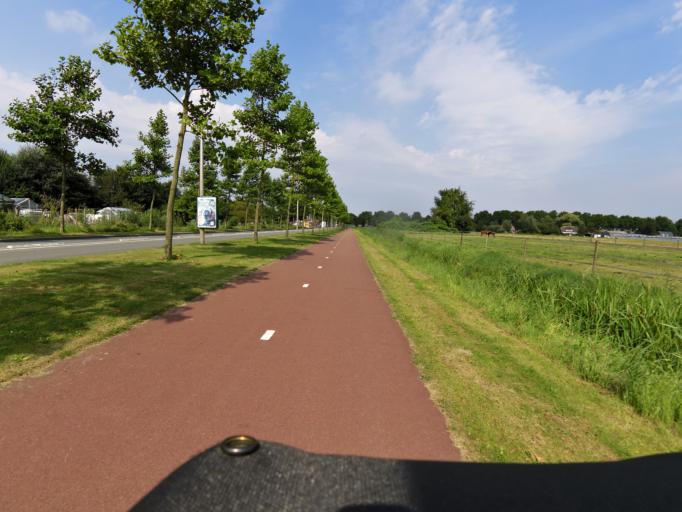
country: NL
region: South Holland
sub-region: Gemeente Binnenmaas
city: Heinenoord
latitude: 51.8220
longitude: 4.4784
